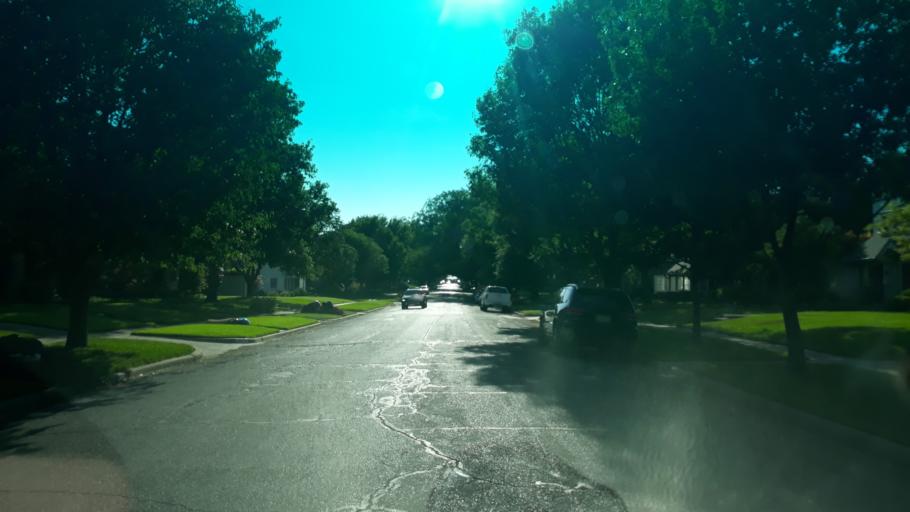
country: US
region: Texas
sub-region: Dallas County
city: Highland Park
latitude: 32.8299
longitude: -96.7626
